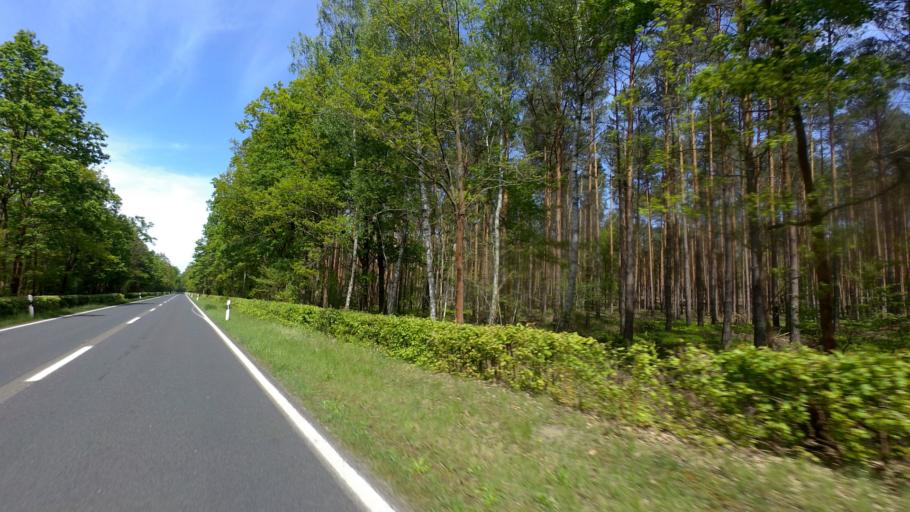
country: DE
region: Brandenburg
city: Sperenberg
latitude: 52.1213
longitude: 13.3685
